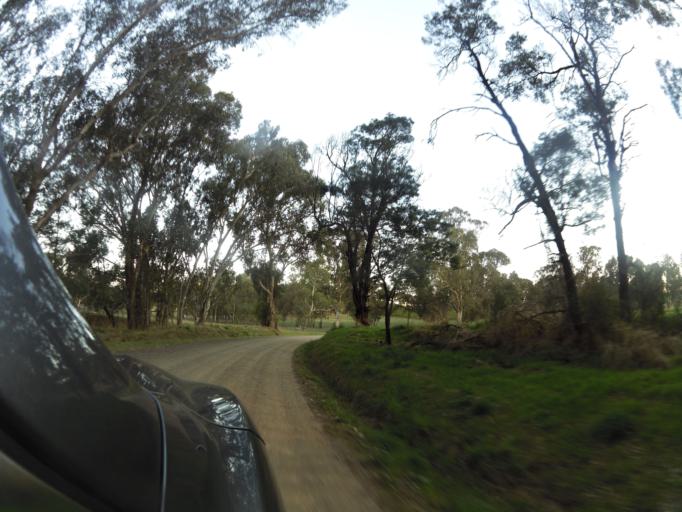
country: AU
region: Victoria
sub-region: Murrindindi
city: Alexandra
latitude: -37.1475
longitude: 145.5276
